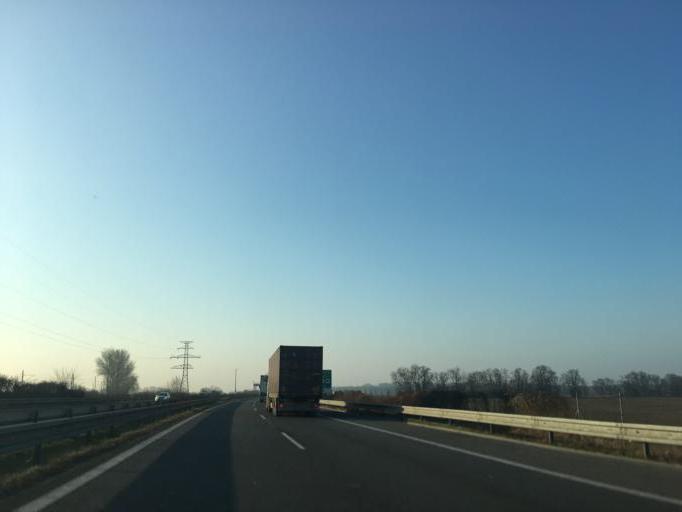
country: AT
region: Burgenland
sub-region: Politischer Bezirk Neusiedl am See
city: Kittsee
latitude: 48.0963
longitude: 17.0984
